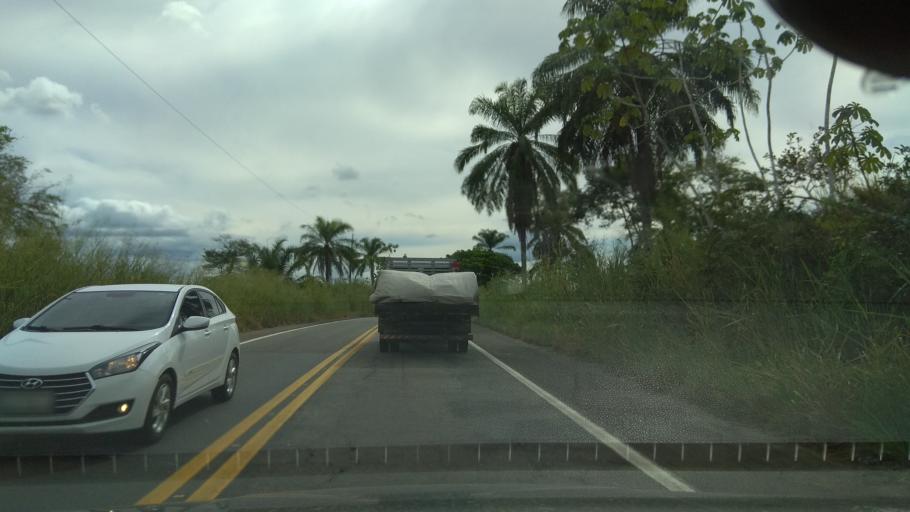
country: BR
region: Bahia
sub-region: Ipiau
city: Ipiau
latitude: -14.1932
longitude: -39.6514
